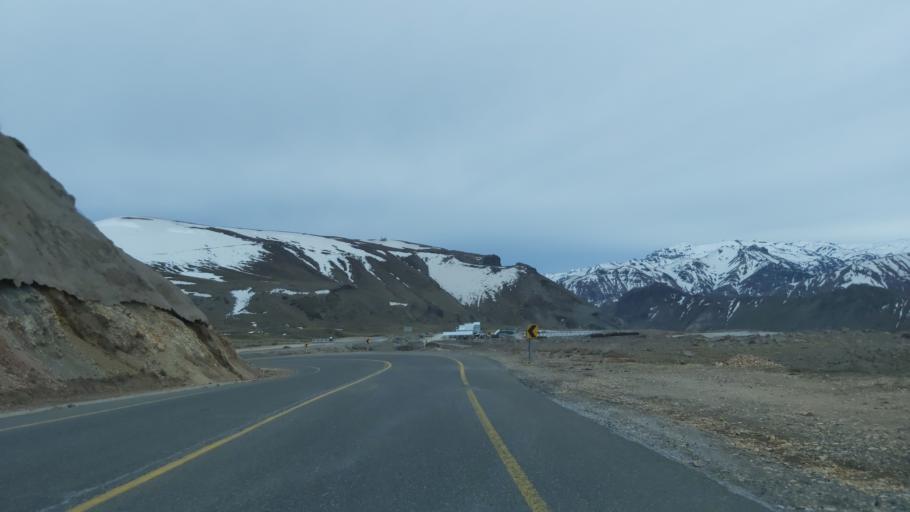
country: CL
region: Maule
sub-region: Provincia de Linares
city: Colbun
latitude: -35.9722
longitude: -70.5649
